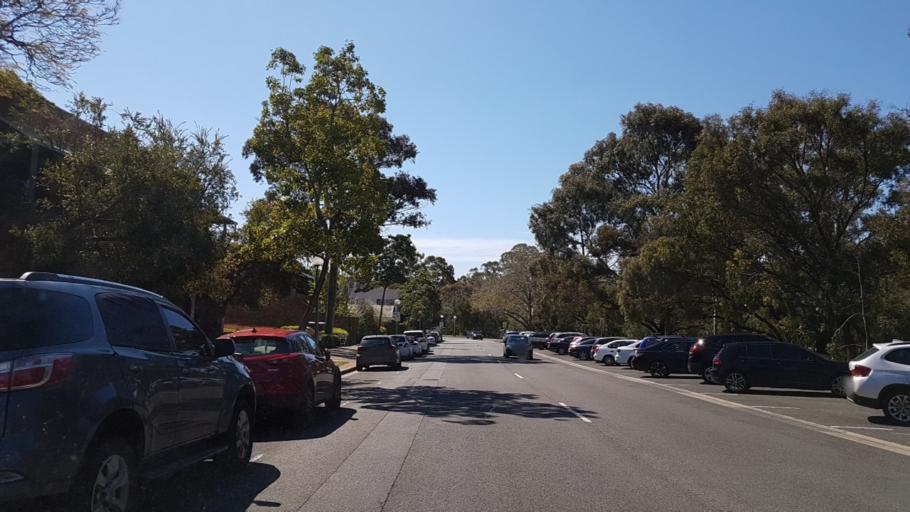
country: AU
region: South Australia
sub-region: Adelaide
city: Adelaide
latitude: -34.9305
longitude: 138.6168
